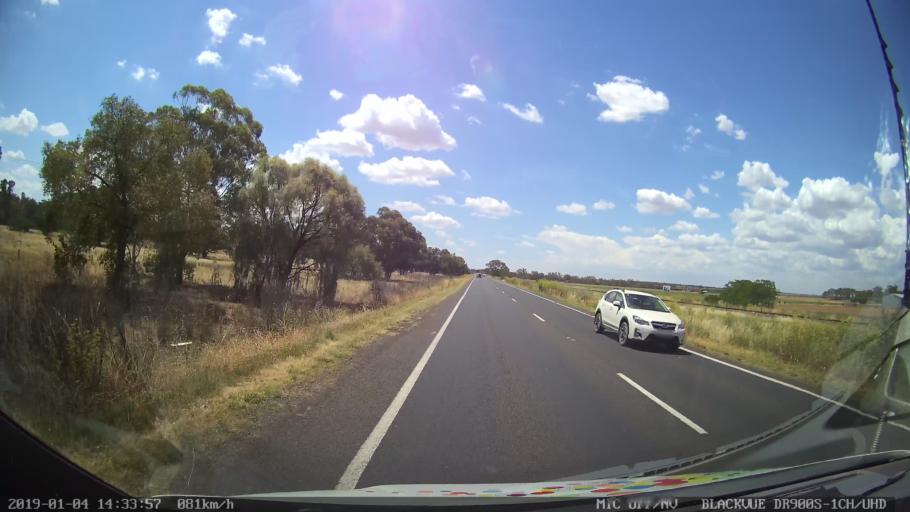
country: AU
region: New South Wales
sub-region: Dubbo Municipality
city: Dubbo
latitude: -32.2046
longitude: 148.6192
